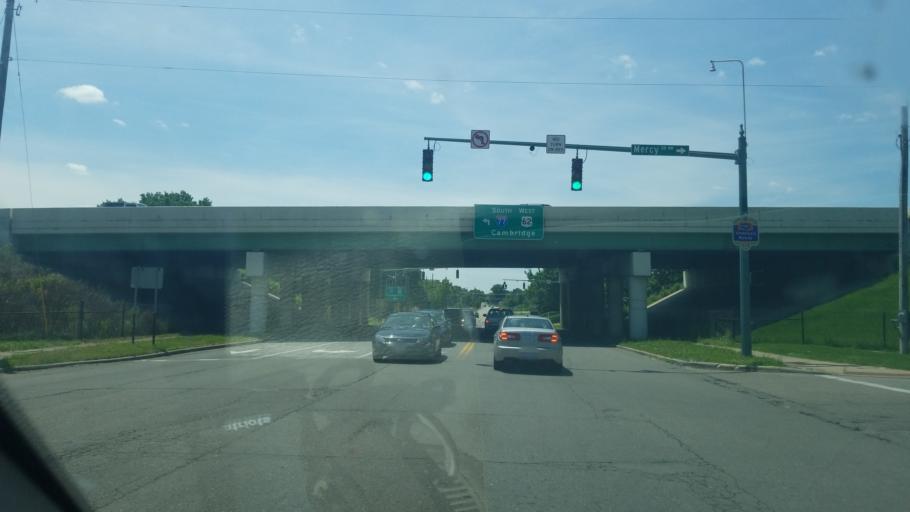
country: US
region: Ohio
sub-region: Stark County
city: Canton
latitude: 40.8114
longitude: -81.3970
